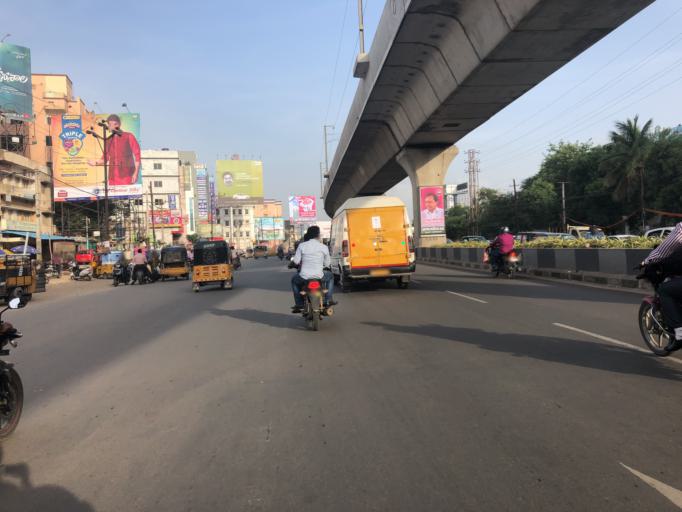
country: IN
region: Telangana
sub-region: Rangareddi
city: Kukatpalli
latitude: 17.4825
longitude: 78.4148
